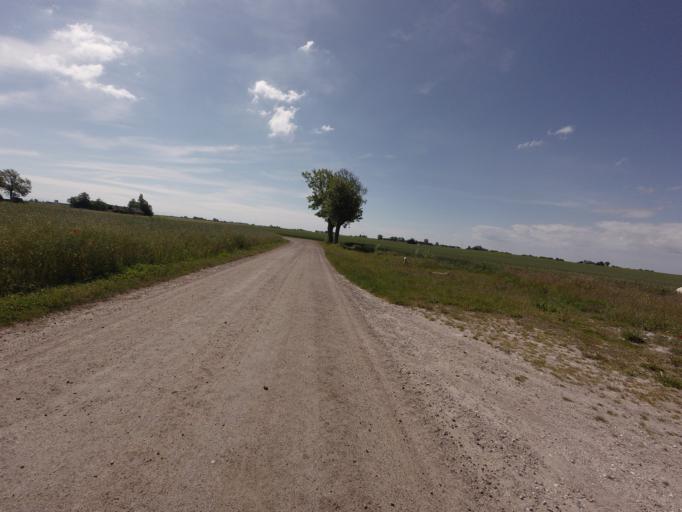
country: SE
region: Skane
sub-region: Trelleborgs Kommun
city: Skare
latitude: 55.4129
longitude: 13.0503
